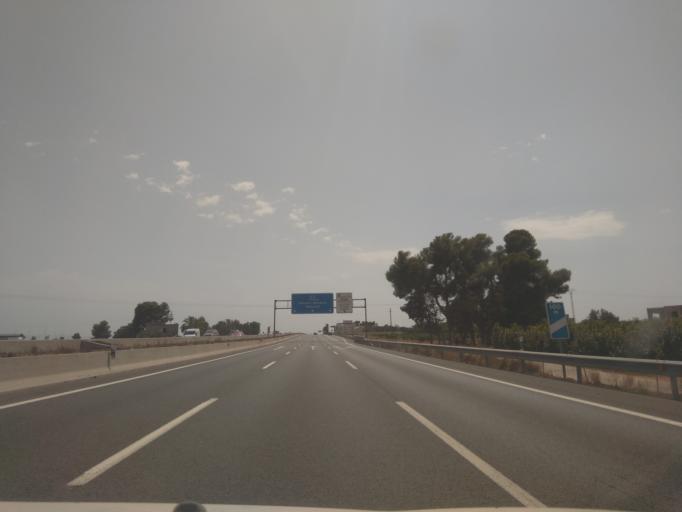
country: ES
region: Valencia
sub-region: Provincia de Valencia
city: Alginet
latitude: 39.2914
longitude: -0.4534
